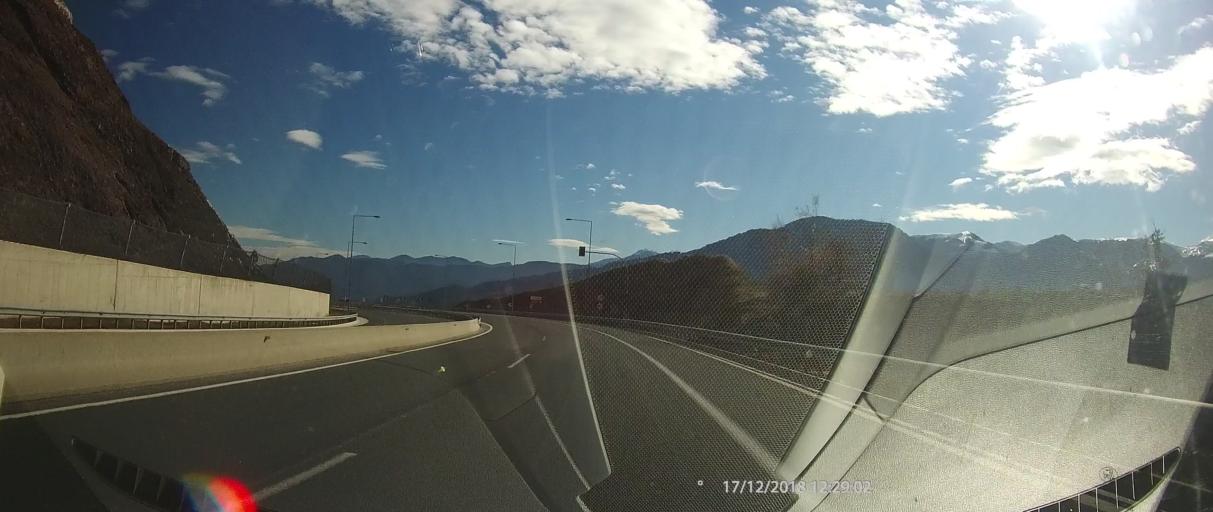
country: GR
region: Epirus
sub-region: Nomos Ioanninon
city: Metsovo
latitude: 39.7857
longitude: 21.2852
